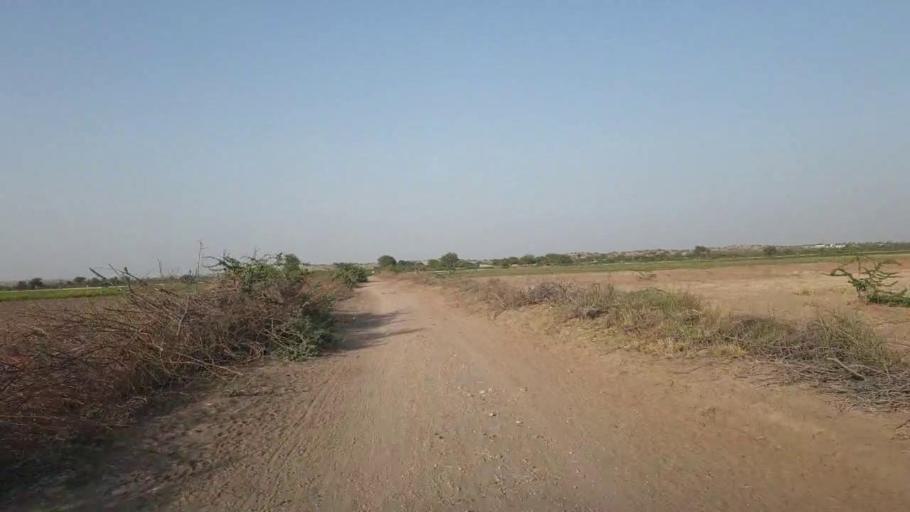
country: PK
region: Sindh
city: Dhoro Naro
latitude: 25.4985
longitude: 69.5848
